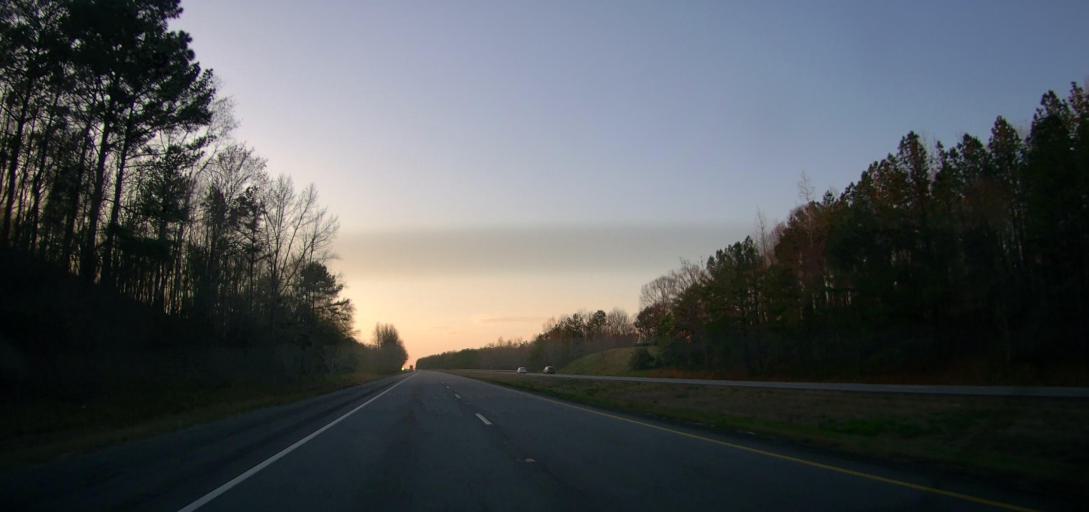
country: US
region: Alabama
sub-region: Coosa County
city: Goodwater
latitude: 33.0107
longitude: -86.0932
